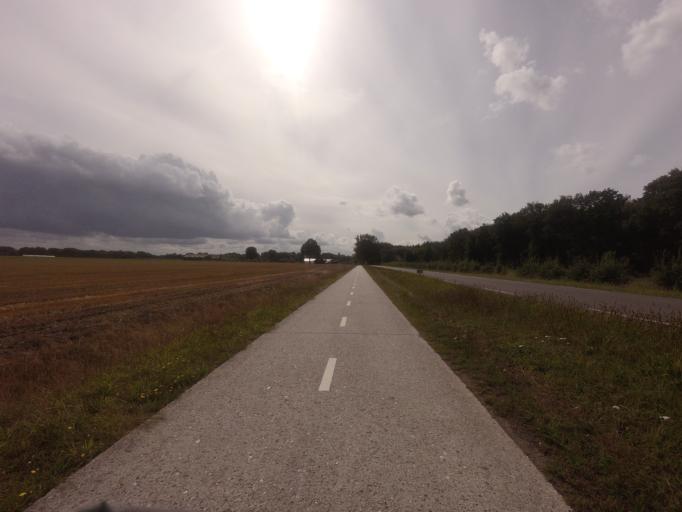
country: NL
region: Drenthe
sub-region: Gemeente Assen
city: Assen
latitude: 53.0523
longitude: 6.4560
